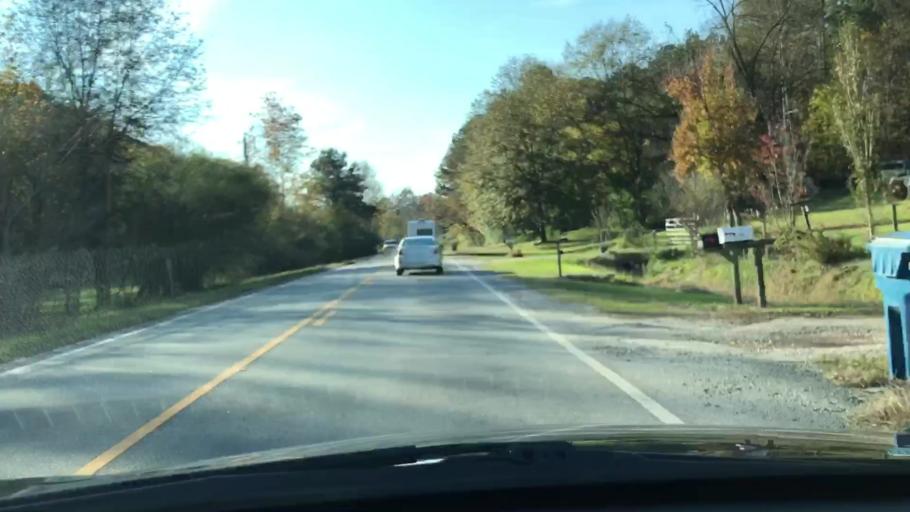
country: US
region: Alabama
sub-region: Cleburne County
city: Heflin
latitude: 33.6500
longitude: -85.5447
